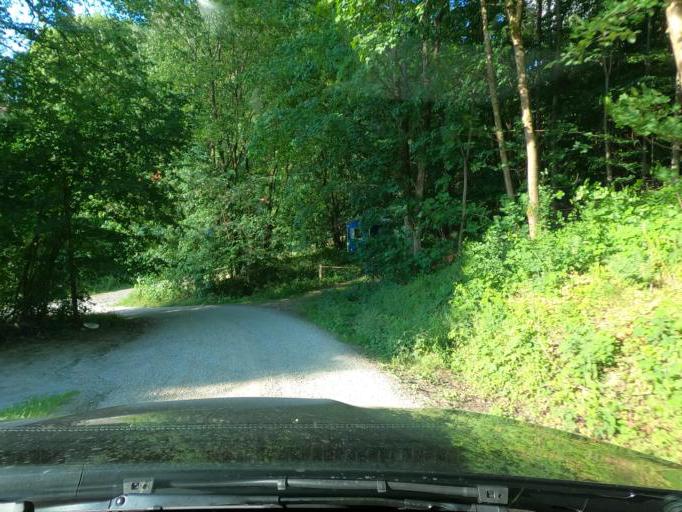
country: DE
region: Lower Saxony
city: Osterode am Harz
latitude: 51.7473
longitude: 10.2934
